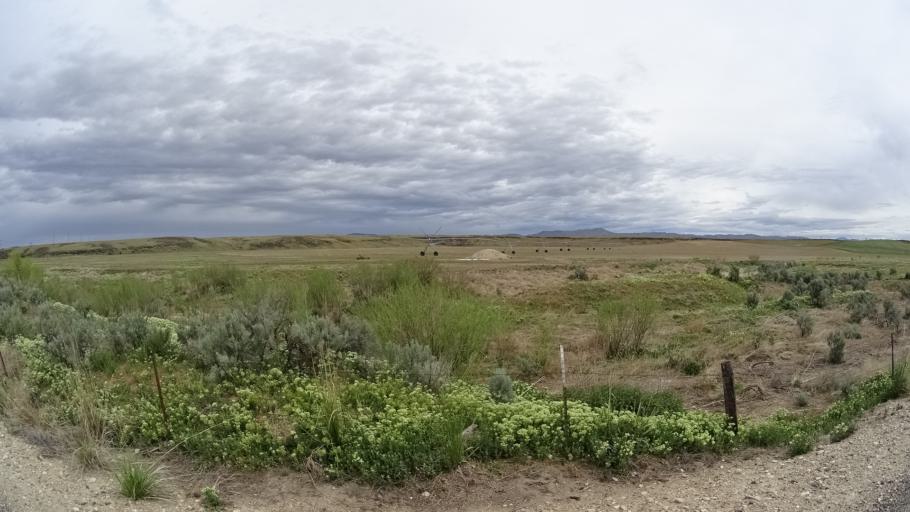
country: US
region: Idaho
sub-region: Ada County
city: Boise
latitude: 43.3890
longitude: -115.9832
